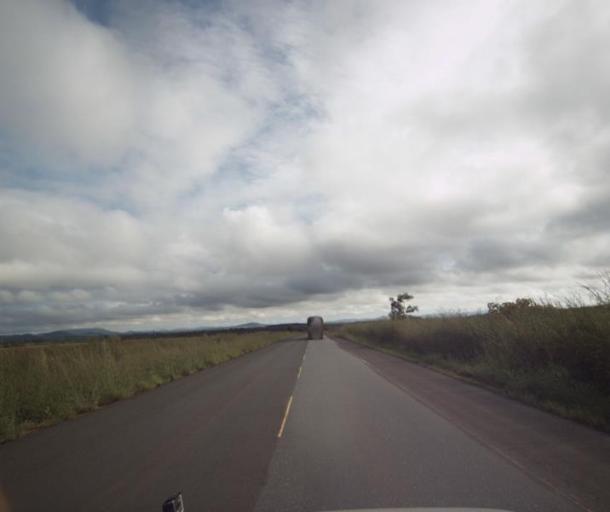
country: BR
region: Goias
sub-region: Padre Bernardo
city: Padre Bernardo
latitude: -15.3511
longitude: -48.6469
